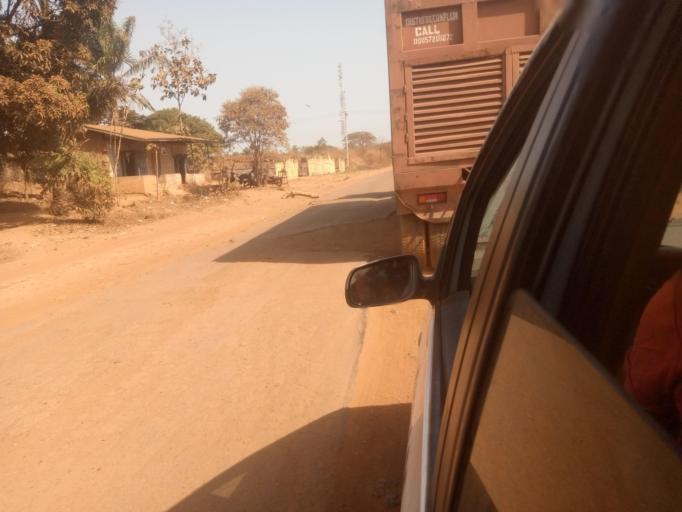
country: NG
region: Enugu
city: Obollo-Afor
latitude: 6.9660
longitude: 7.5343
